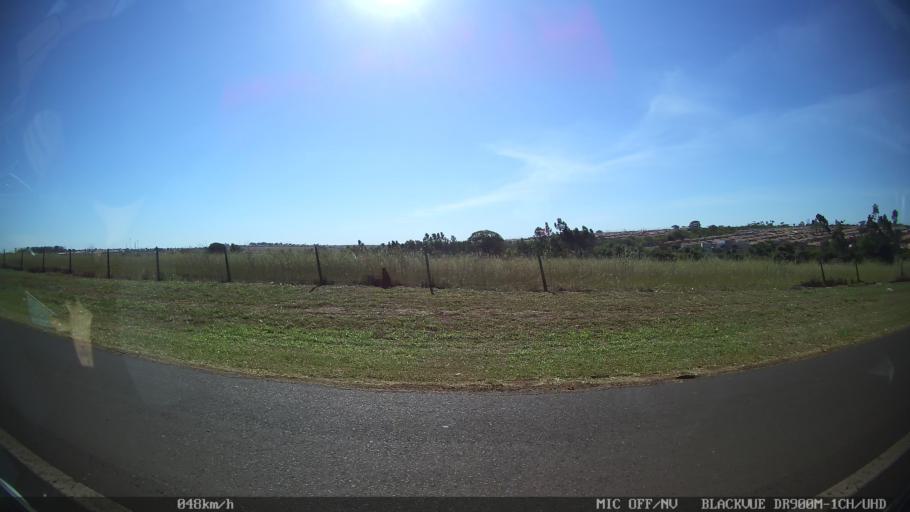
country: BR
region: Sao Paulo
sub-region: Olimpia
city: Olimpia
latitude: -20.7368
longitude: -48.8796
